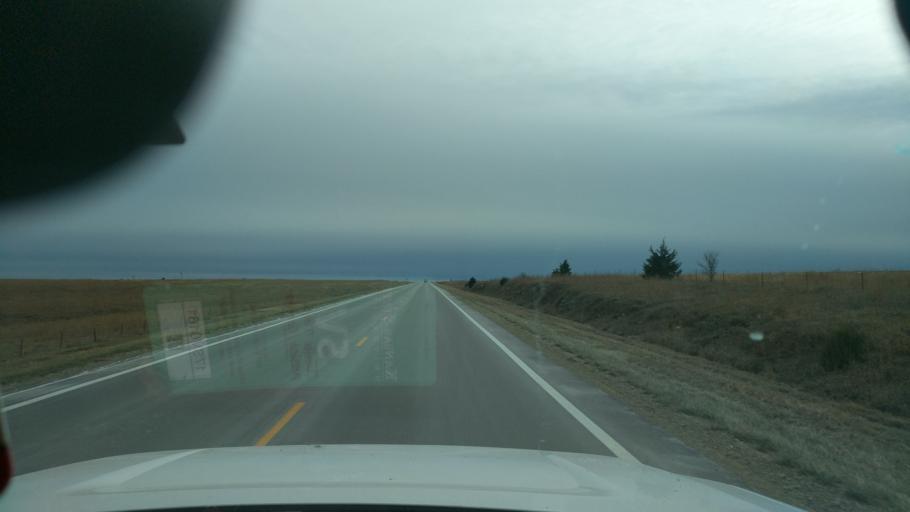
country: US
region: Kansas
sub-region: Geary County
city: Junction City
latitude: 38.8756
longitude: -96.8531
